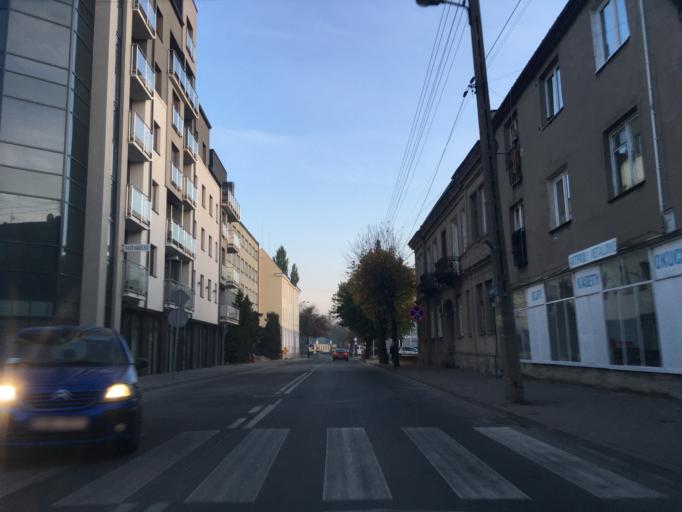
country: PL
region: Lodz Voivodeship
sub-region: Skierniewice
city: Skierniewice
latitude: 51.9593
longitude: 20.1449
